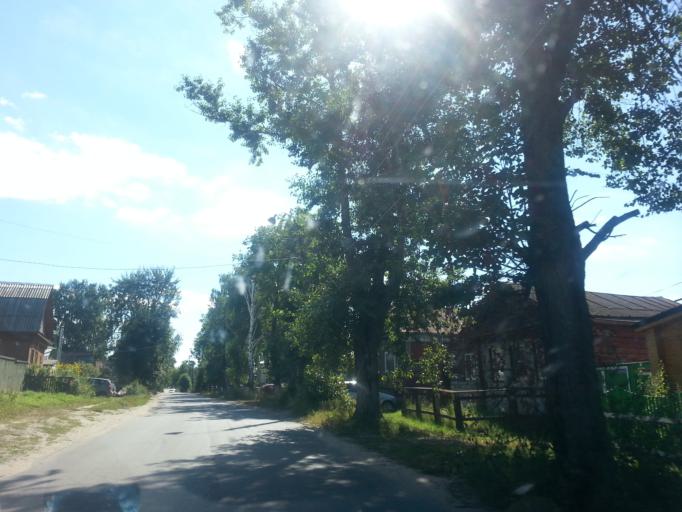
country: RU
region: Nizjnij Novgorod
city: Taremskoye
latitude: 55.9937
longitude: 43.0135
